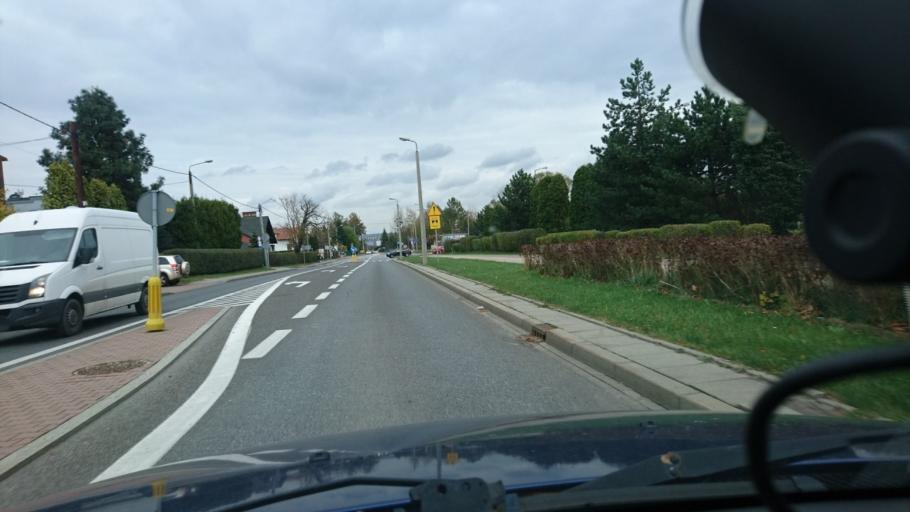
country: PL
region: Silesian Voivodeship
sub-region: Bielsko-Biala
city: Bielsko-Biala
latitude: 49.7933
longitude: 19.0376
